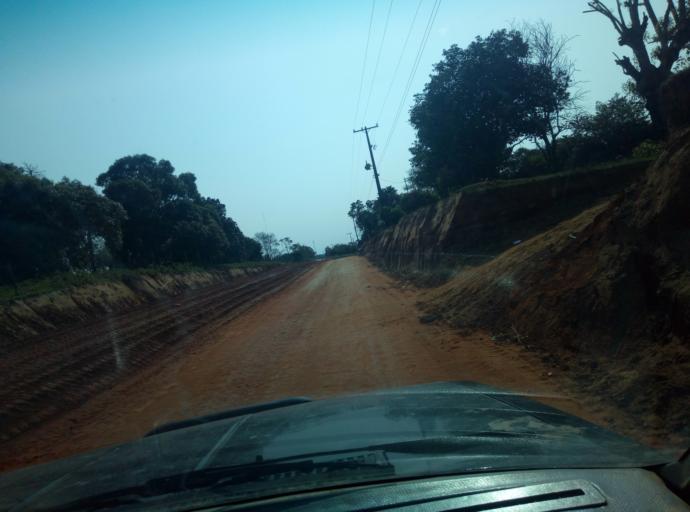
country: PY
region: Caaguazu
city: Carayao
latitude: -25.3275
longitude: -56.3307
